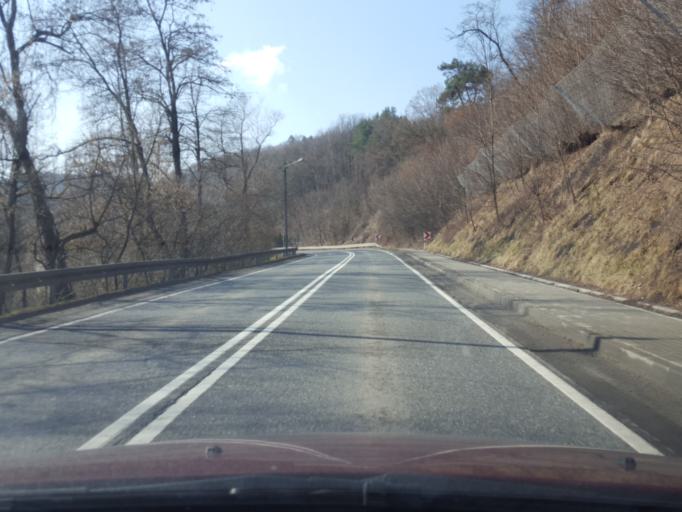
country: PL
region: Lesser Poland Voivodeship
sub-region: Powiat brzeski
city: Czchow
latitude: 49.8310
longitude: 20.6778
